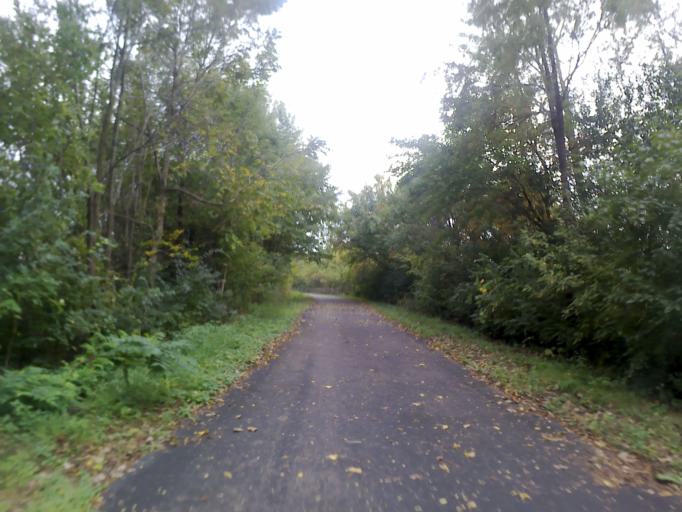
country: US
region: Illinois
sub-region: DuPage County
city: Warrenville
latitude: 41.8106
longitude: -88.1745
